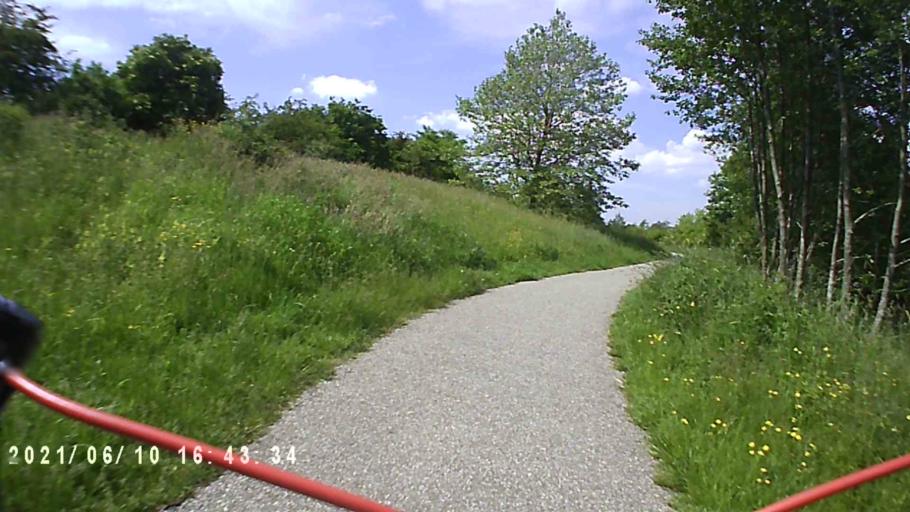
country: NL
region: Friesland
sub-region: Gemeente Achtkarspelen
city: Buitenpost
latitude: 53.2485
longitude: 6.1337
